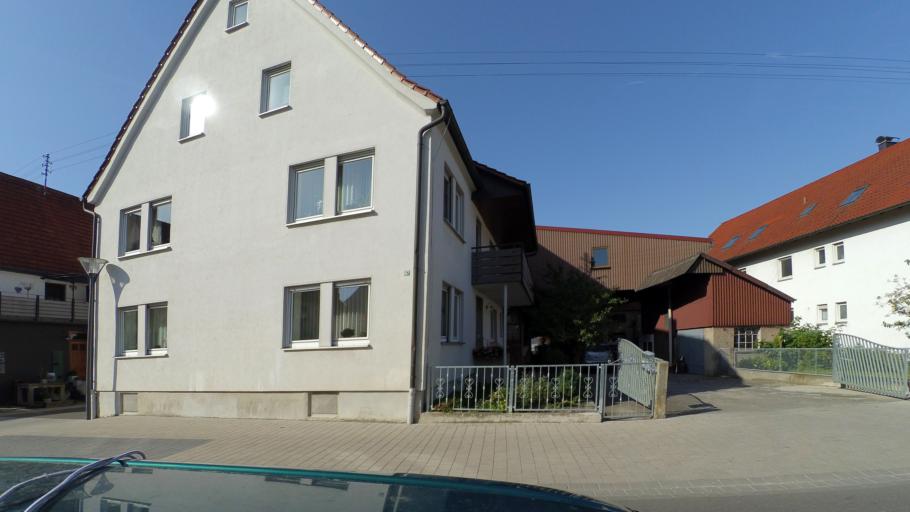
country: DE
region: Baden-Wuerttemberg
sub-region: Regierungsbezirk Stuttgart
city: Sontheim an der Brenz
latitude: 48.5518
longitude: 10.2922
